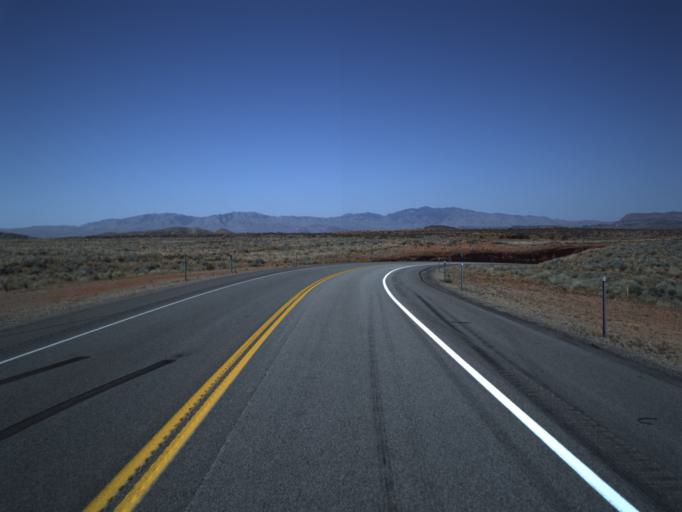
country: US
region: Utah
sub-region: Washington County
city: Washington
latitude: 37.1101
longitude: -113.4178
